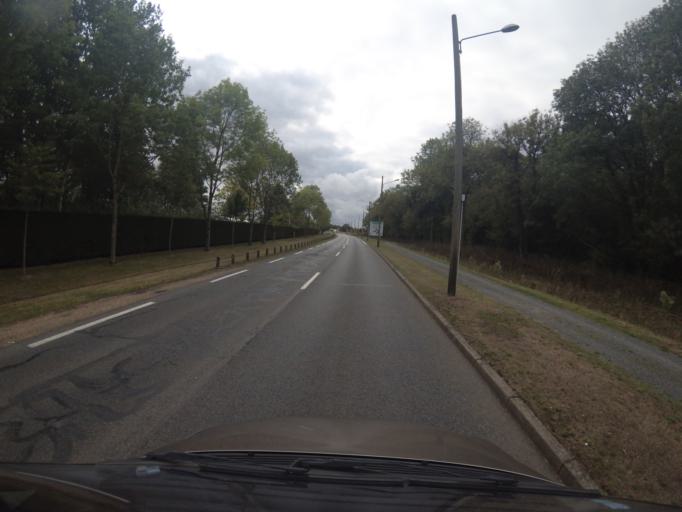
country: FR
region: Ile-de-France
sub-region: Departement de Seine-et-Marne
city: Chessy
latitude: 48.8690
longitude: 2.7656
